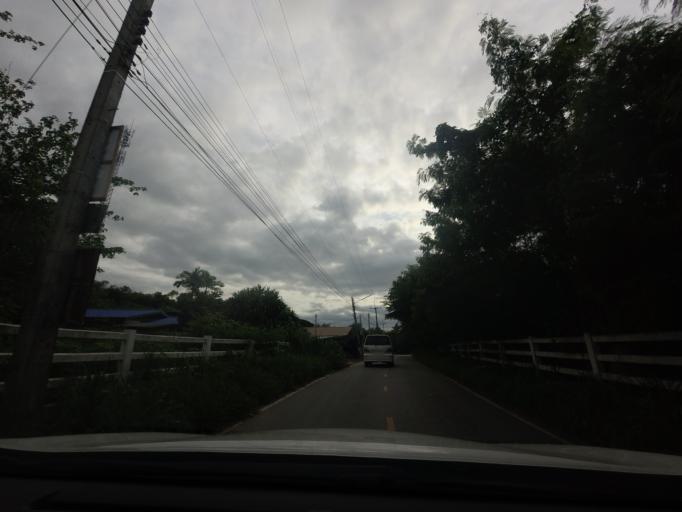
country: TH
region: Nakhon Ratchasima
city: Pak Chong
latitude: 14.6088
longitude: 101.4144
